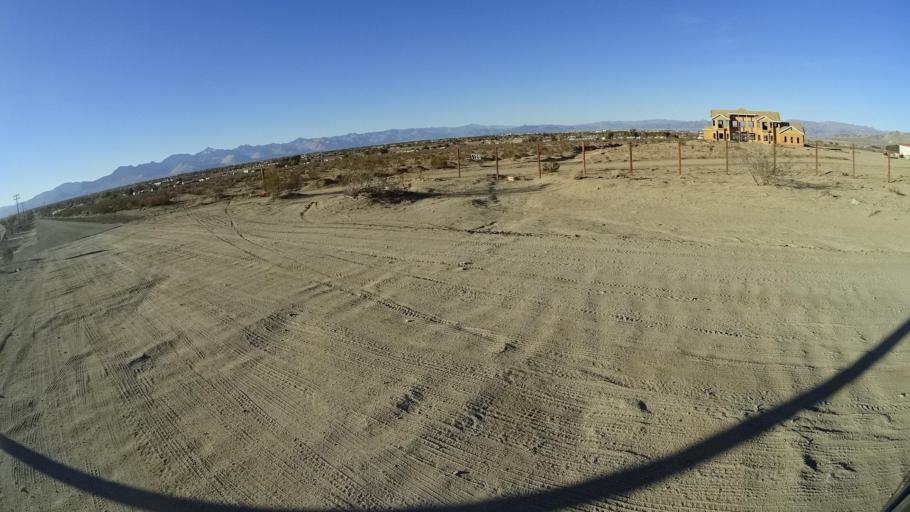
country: US
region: California
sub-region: Kern County
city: Ridgecrest
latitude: 35.6006
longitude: -117.6480
